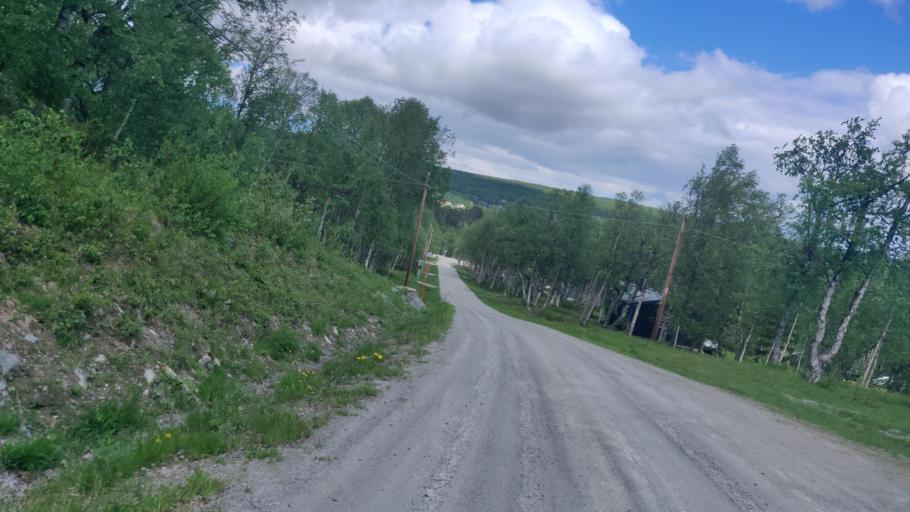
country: NO
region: Sor-Trondelag
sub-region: Tydal
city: Aas
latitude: 62.6424
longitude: 12.4120
